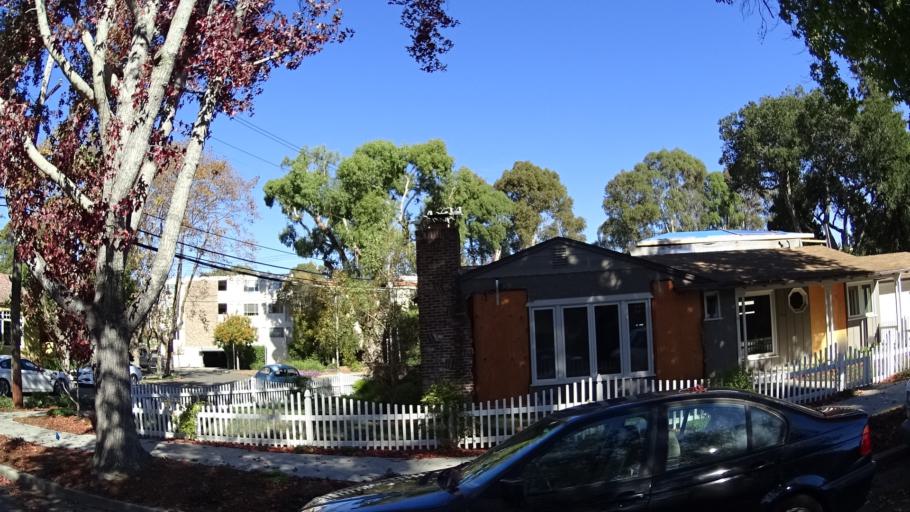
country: US
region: California
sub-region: San Mateo County
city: Burlingame
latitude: 37.5789
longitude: -122.3591
